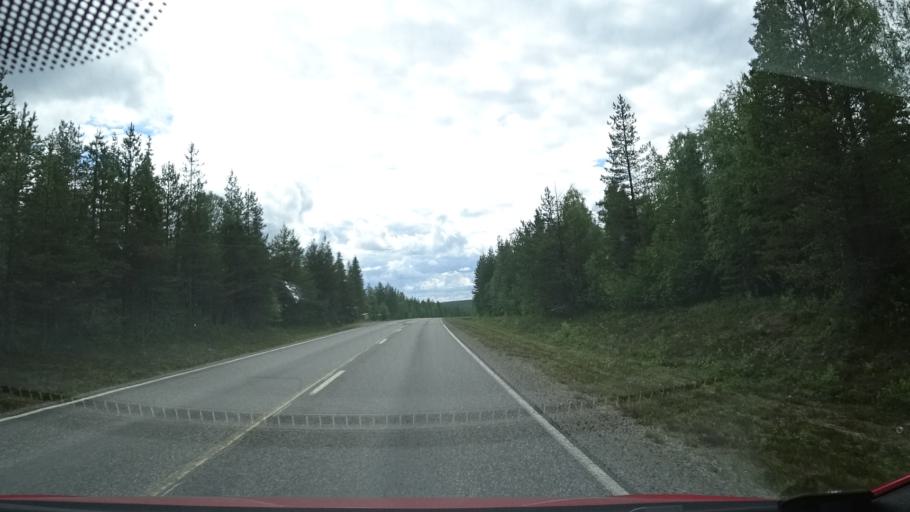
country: FI
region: Lapland
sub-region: Tunturi-Lappi
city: Kittilae
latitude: 67.5534
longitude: 24.9217
